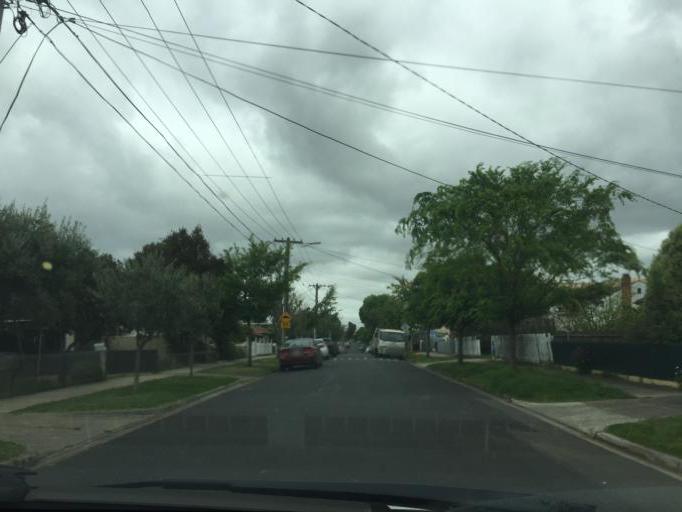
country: AU
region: Victoria
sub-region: Hobsons Bay
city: South Kingsville
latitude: -37.8206
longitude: 144.8776
